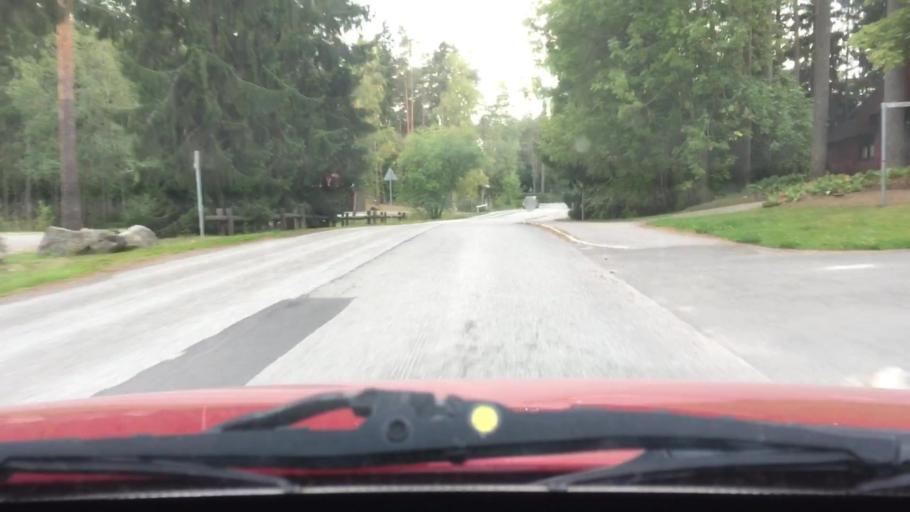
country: FI
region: Varsinais-Suomi
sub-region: Turku
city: Masku
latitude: 60.5515
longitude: 22.1344
